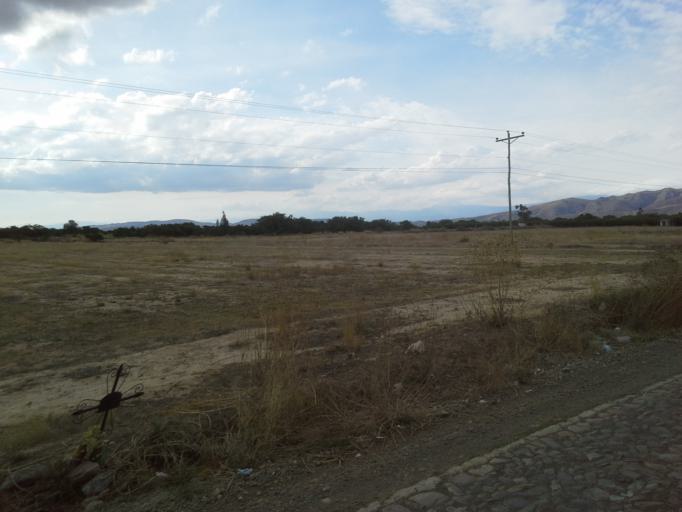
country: BO
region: Cochabamba
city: Tarata
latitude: -17.5906
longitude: -66.0184
